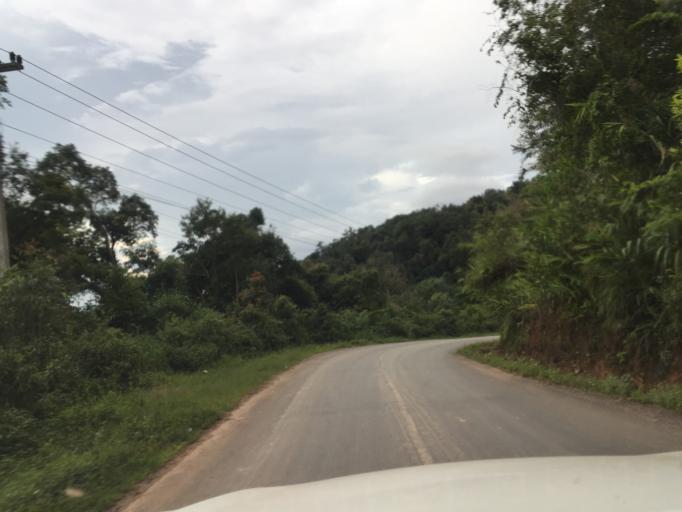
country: LA
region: Phongsali
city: Phongsali
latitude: 21.3297
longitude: 102.0531
